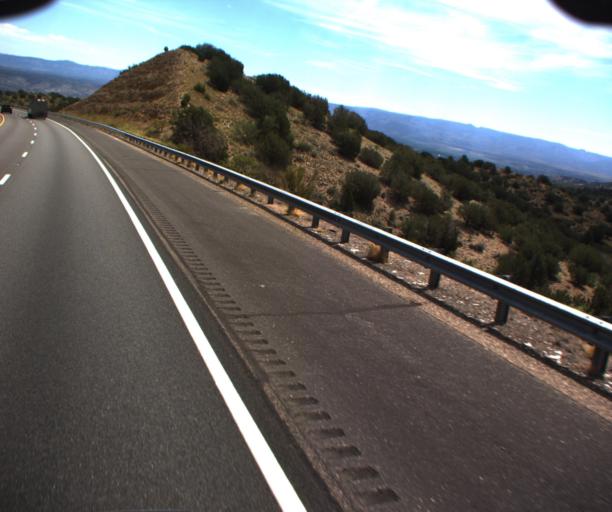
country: US
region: Arizona
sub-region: Yavapai County
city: Camp Verde
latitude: 34.5380
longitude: -111.9120
